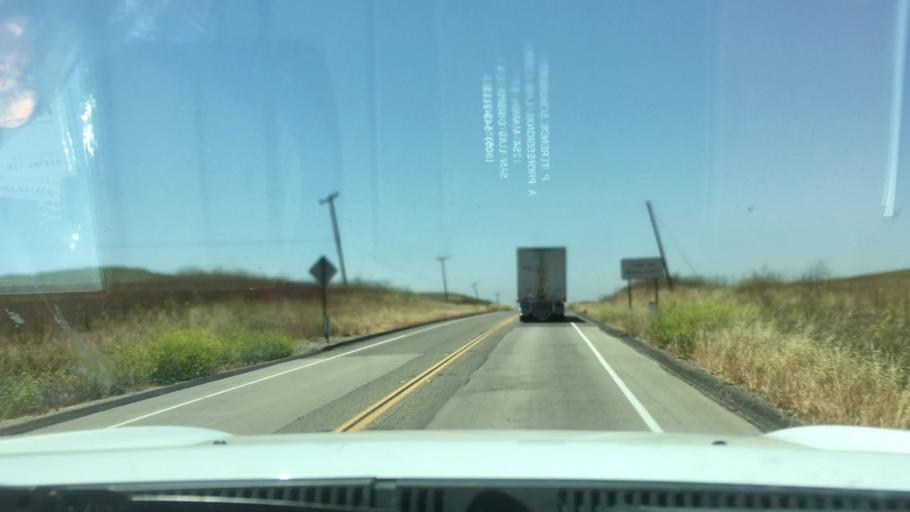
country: US
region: California
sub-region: Santa Barbara County
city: Santa Maria
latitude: 34.9983
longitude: -120.3835
